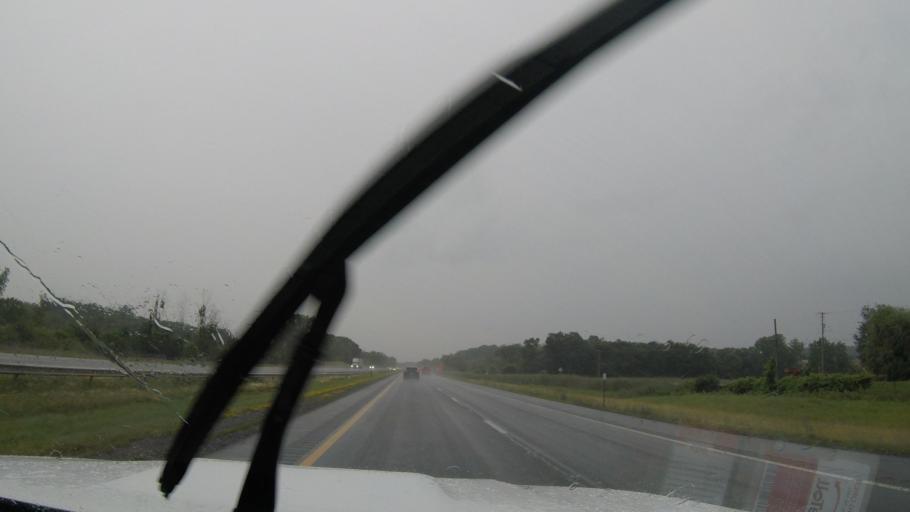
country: US
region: New York
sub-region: Seneca County
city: Bridgeport
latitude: 43.0022
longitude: -76.7138
